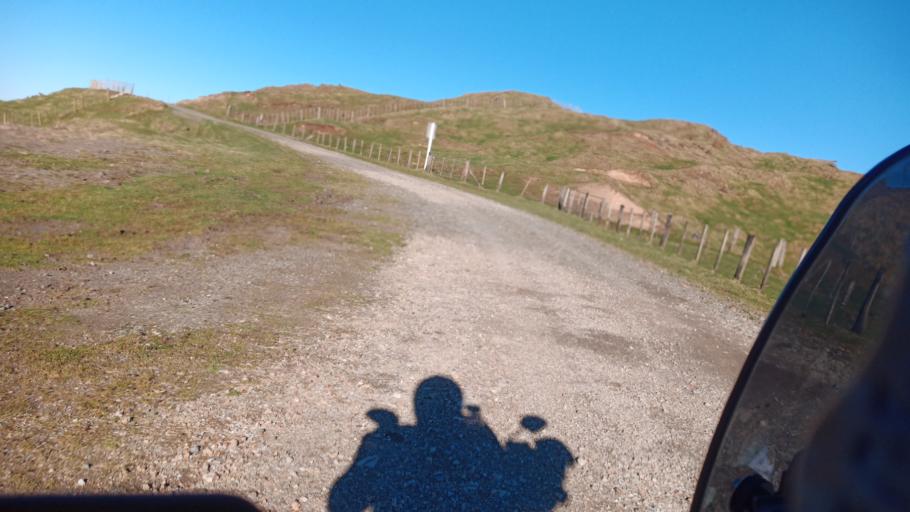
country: NZ
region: Gisborne
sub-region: Gisborne District
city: Gisborne
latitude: -38.1306
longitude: 177.8661
